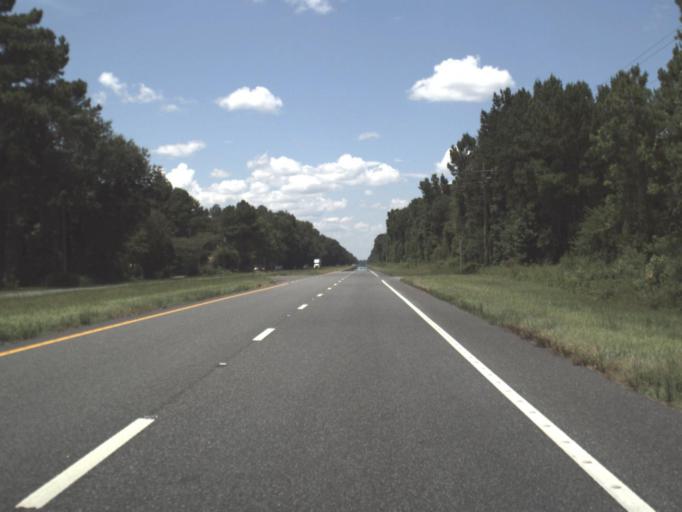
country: US
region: Florida
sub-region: Taylor County
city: Perry
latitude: 30.2771
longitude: -83.7243
